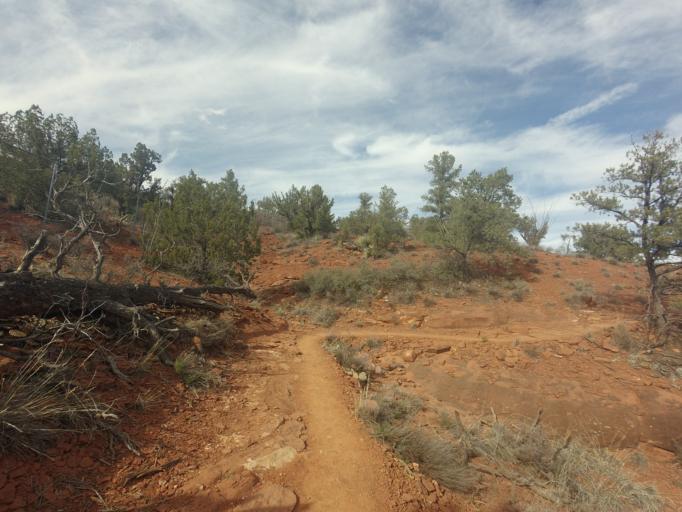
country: US
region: Arizona
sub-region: Yavapai County
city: West Sedona
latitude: 34.8092
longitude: -111.8327
